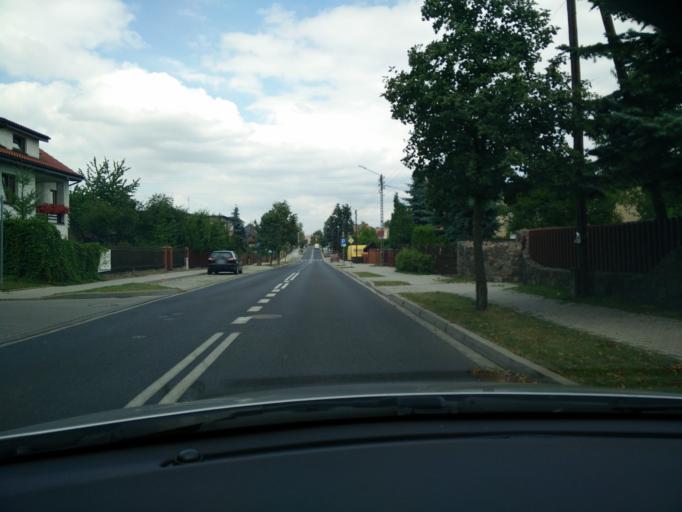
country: PL
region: Greater Poland Voivodeship
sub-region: Powiat sredzki
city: Sroda Wielkopolska
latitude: 52.2274
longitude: 17.2863
